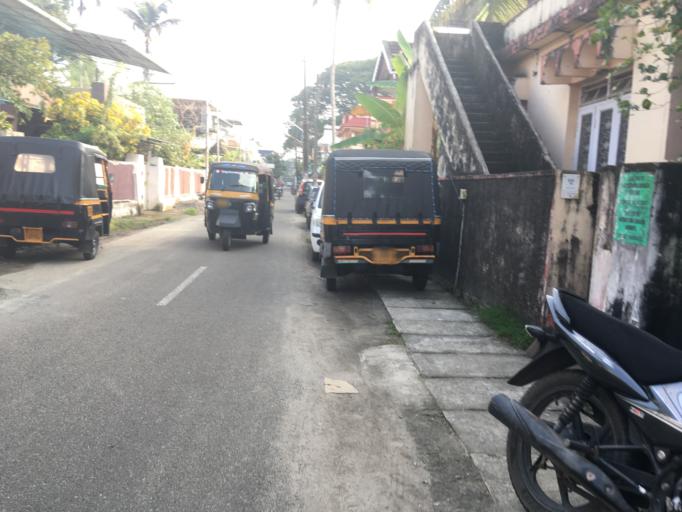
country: IN
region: Kerala
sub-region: Ernakulam
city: Cochin
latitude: 9.9586
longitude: 76.2405
